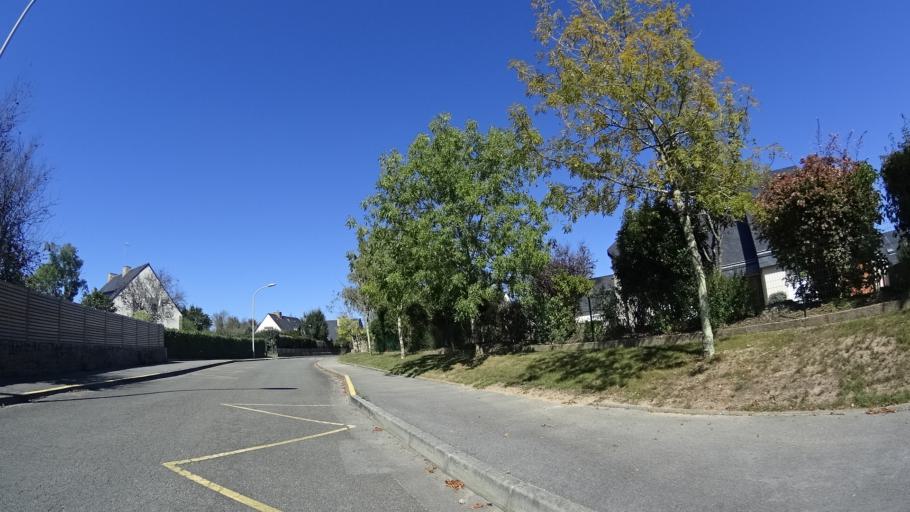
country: FR
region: Brittany
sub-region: Departement du Morbihan
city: Vannes
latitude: 47.6402
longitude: -2.7645
